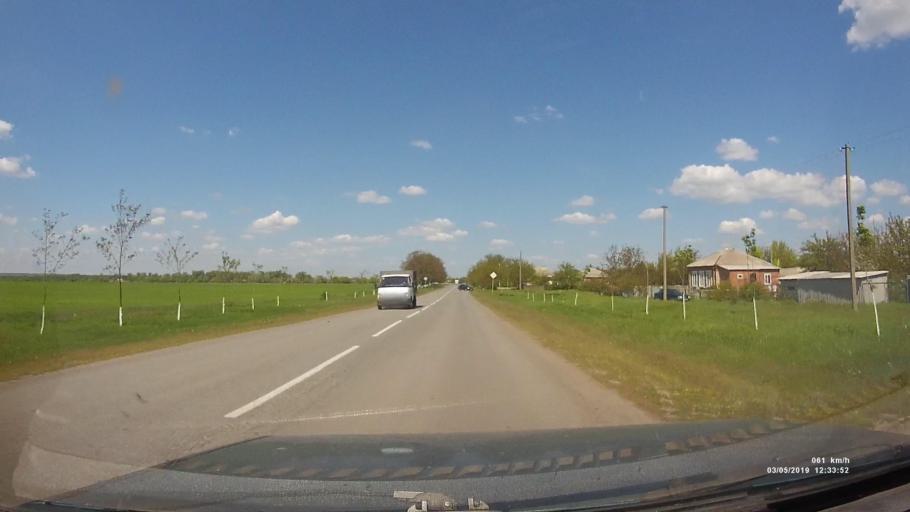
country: RU
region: Rostov
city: Semikarakorsk
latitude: 47.5165
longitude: 40.7710
